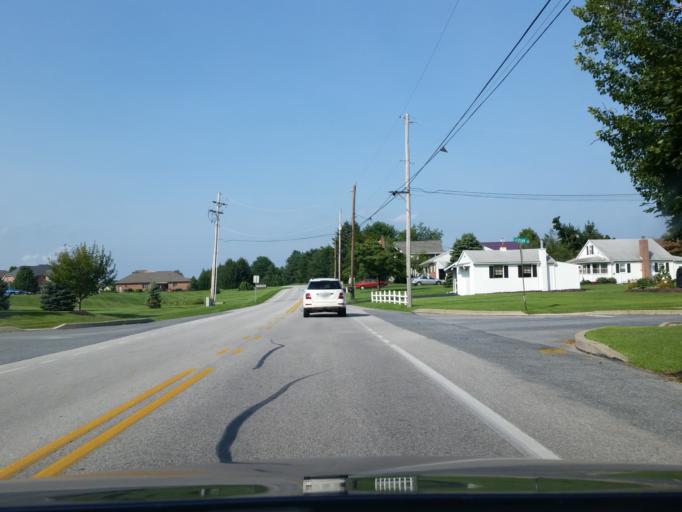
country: US
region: Pennsylvania
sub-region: York County
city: Shiloh
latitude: 39.9912
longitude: -76.7792
